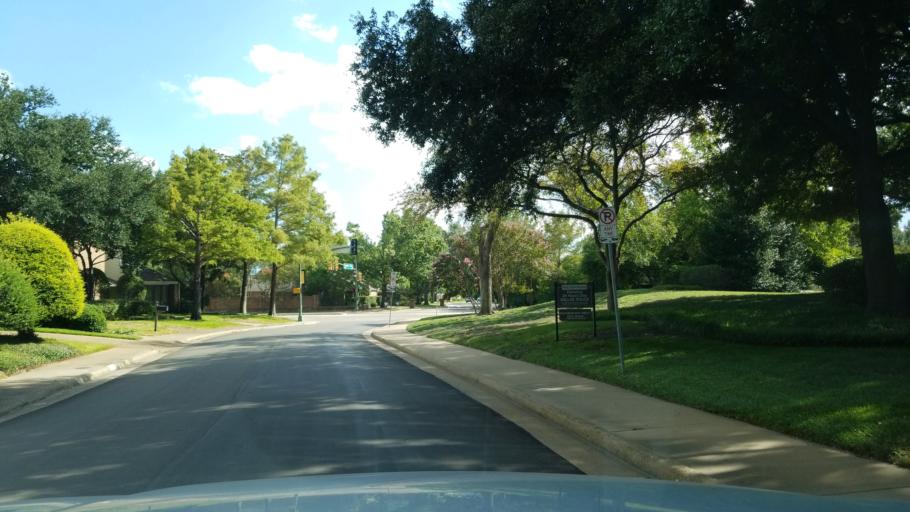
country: US
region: Texas
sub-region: Dallas County
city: Addison
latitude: 32.9630
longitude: -96.7984
